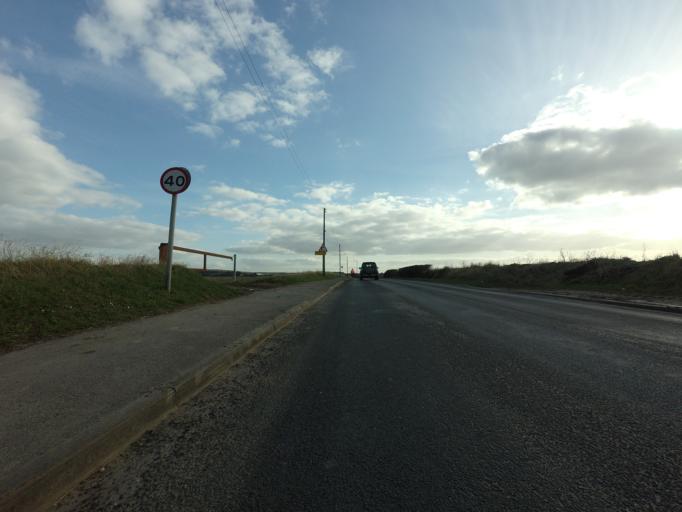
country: GB
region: England
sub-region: Kent
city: Dartford
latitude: 51.4189
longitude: 0.2016
